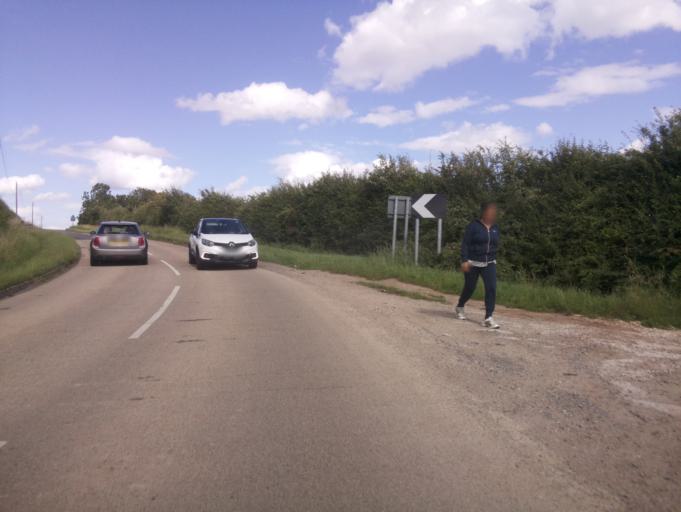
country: GB
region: England
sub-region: Nottinghamshire
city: East Leake
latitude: 52.8244
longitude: -1.1951
